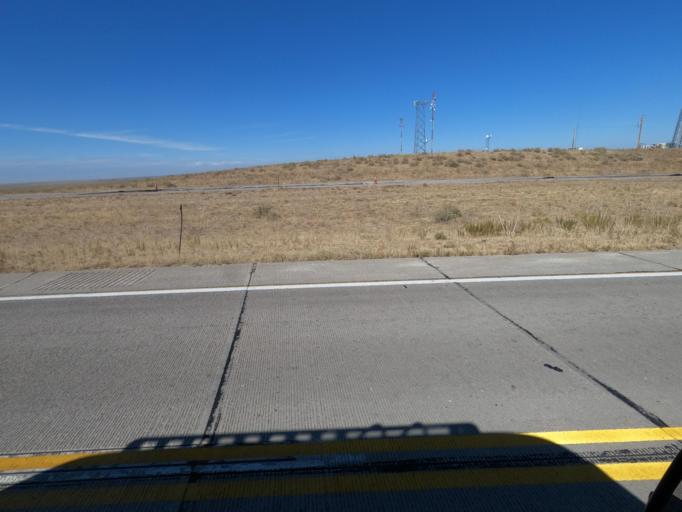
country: US
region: Colorado
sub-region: Weld County
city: Keenesburg
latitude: 40.2252
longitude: -104.1878
